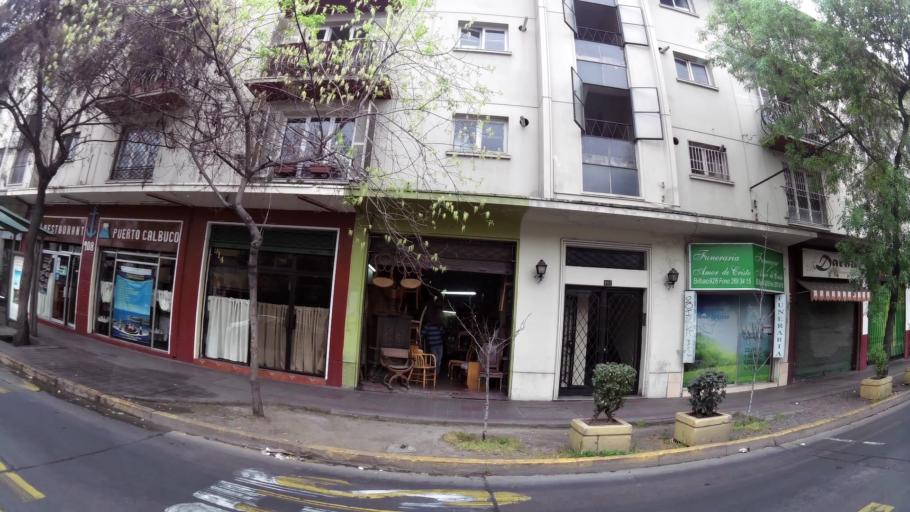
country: CL
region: Santiago Metropolitan
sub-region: Provincia de Santiago
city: Santiago
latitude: -33.4402
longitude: -70.6209
